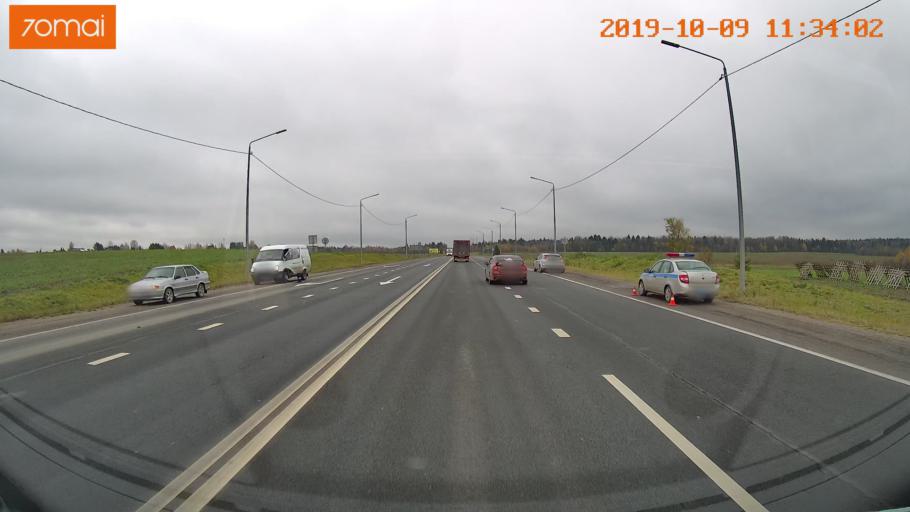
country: RU
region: Vologda
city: Gryazovets
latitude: 59.0198
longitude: 40.1163
